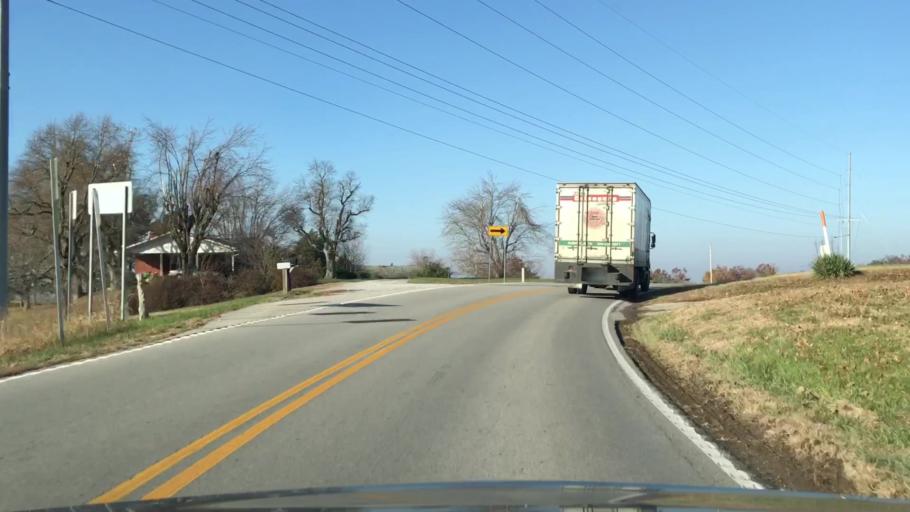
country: US
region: Kentucky
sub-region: Grayson County
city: Leitchfield
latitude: 37.4036
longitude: -86.2425
